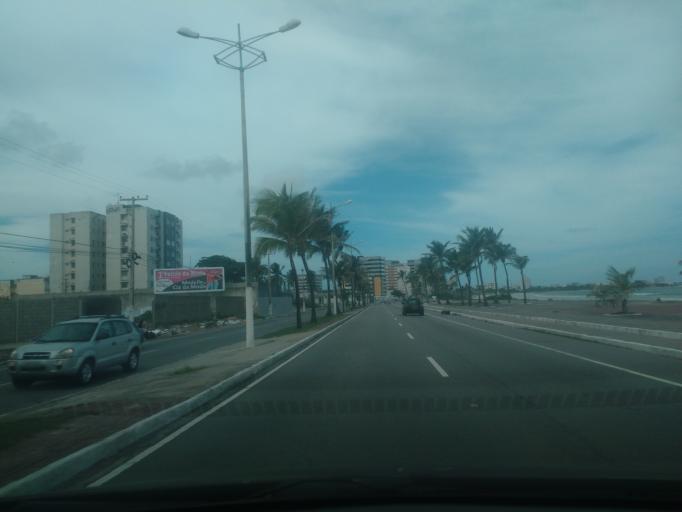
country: BR
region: Alagoas
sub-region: Maceio
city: Maceio
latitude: -9.6715
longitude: -35.7442
